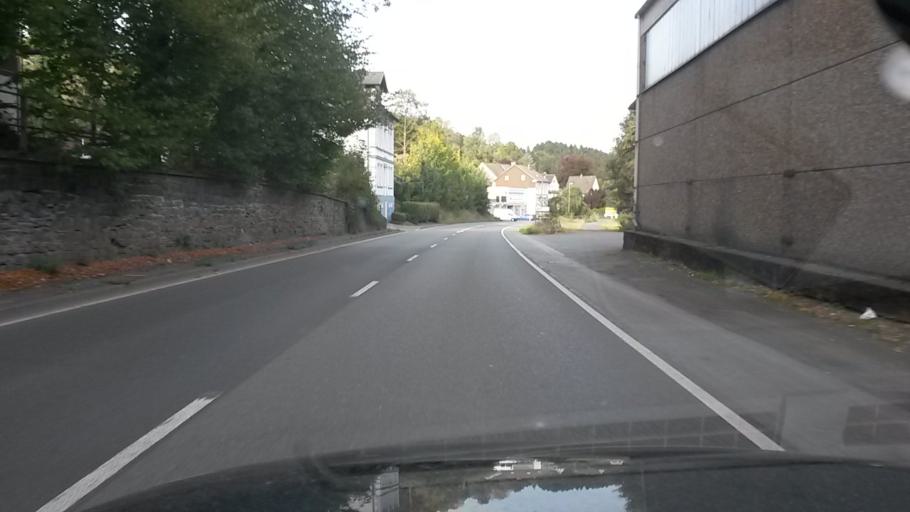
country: DE
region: North Rhine-Westphalia
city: Altena
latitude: 51.2331
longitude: 7.6939
